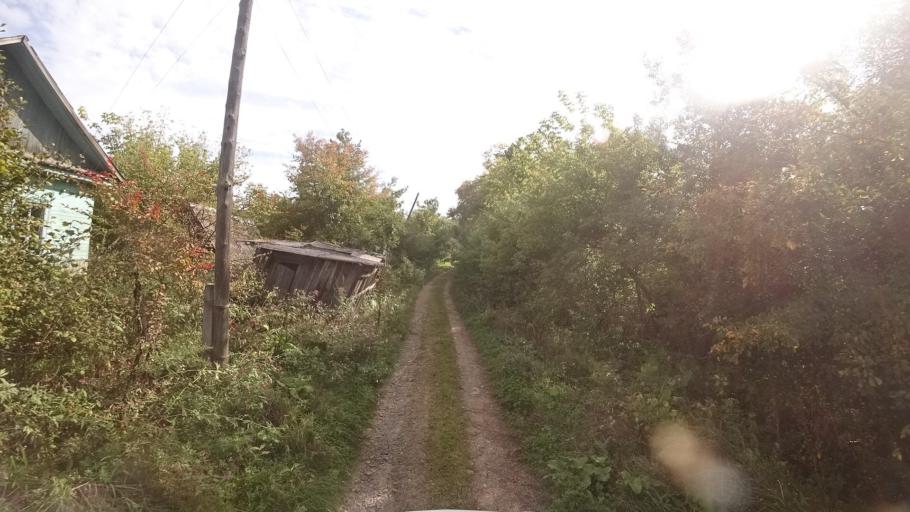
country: RU
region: Primorskiy
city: Dostoyevka
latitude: 44.3258
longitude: 133.4848
